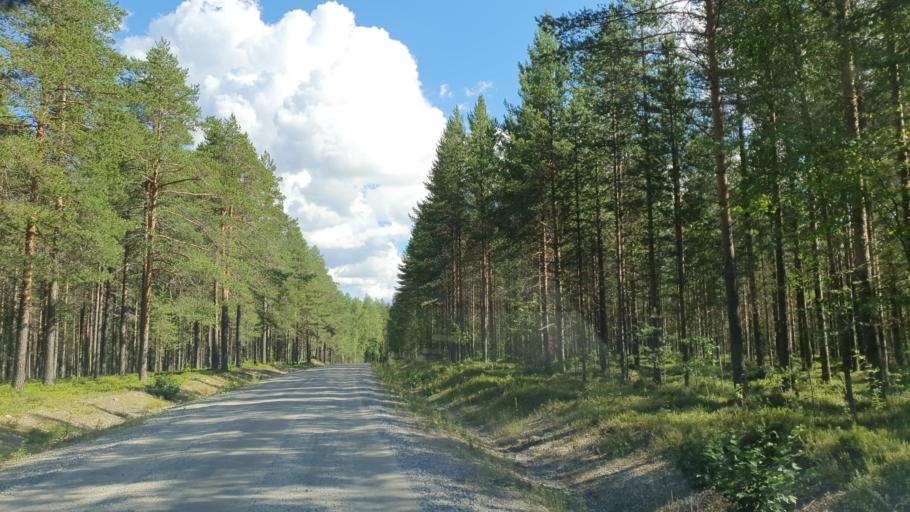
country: FI
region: Kainuu
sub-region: Kehys-Kainuu
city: Kuhmo
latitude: 64.1072
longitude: 29.3914
